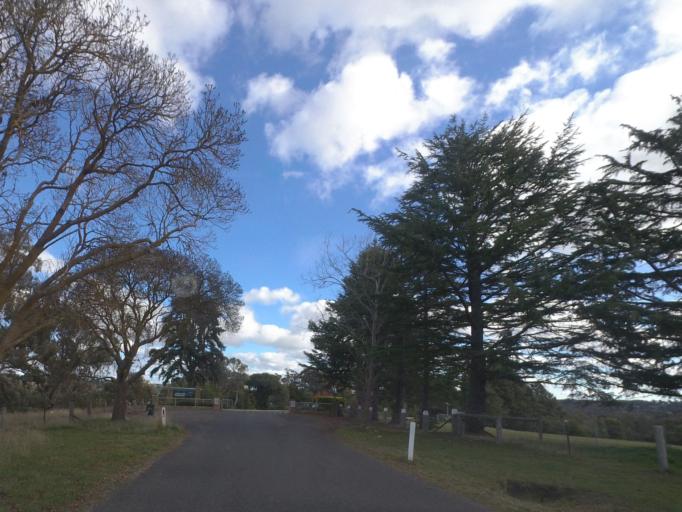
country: AU
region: Victoria
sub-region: Mount Alexander
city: Castlemaine
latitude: -37.2523
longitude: 144.3844
